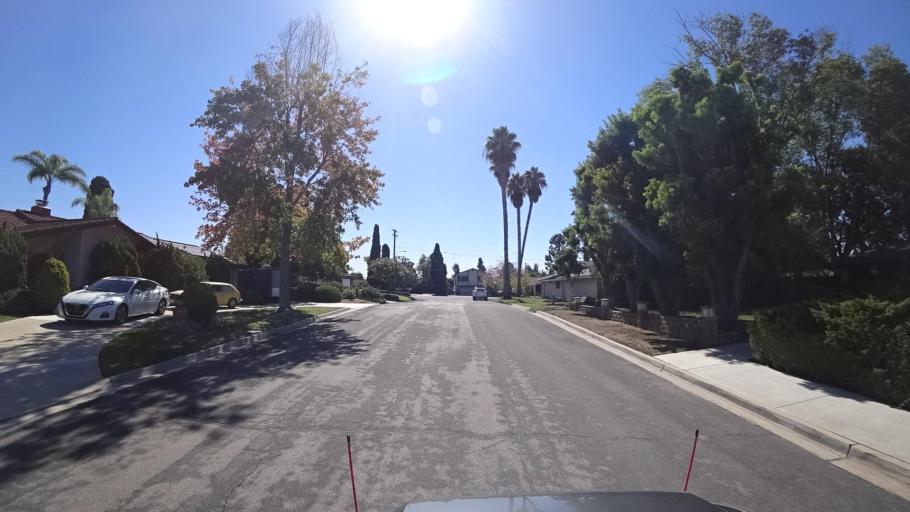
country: US
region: California
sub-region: San Diego County
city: Chula Vista
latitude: 32.6407
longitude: -117.0621
